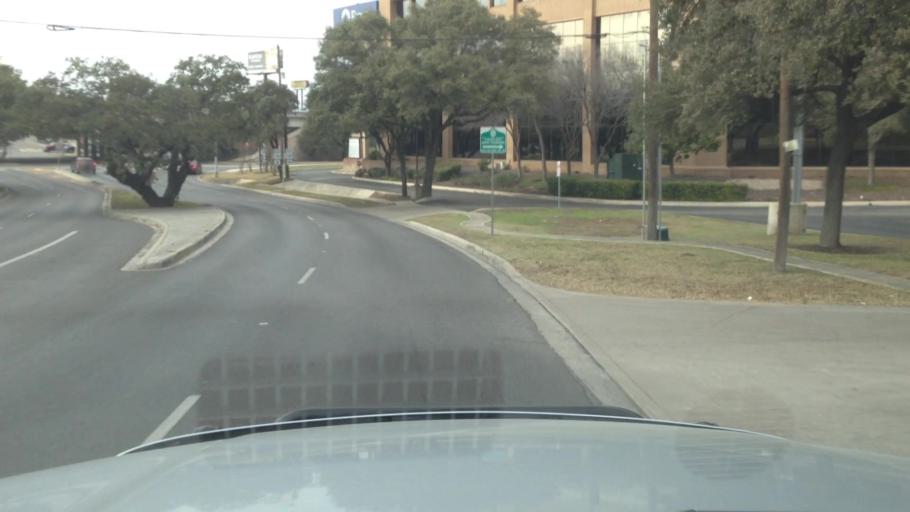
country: US
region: Texas
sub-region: Bexar County
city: Hollywood Park
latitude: 29.5921
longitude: -98.4717
